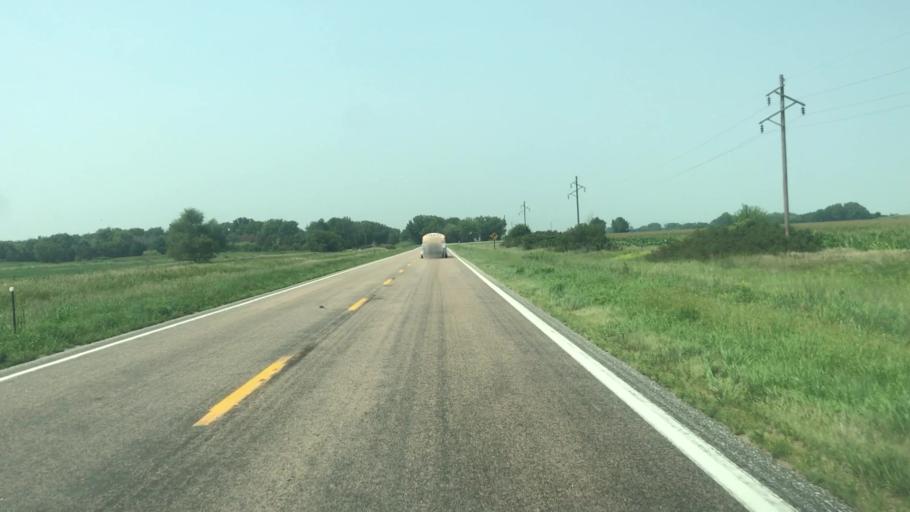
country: US
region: Nebraska
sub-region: Sherman County
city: Loup City
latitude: 41.2313
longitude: -98.9351
